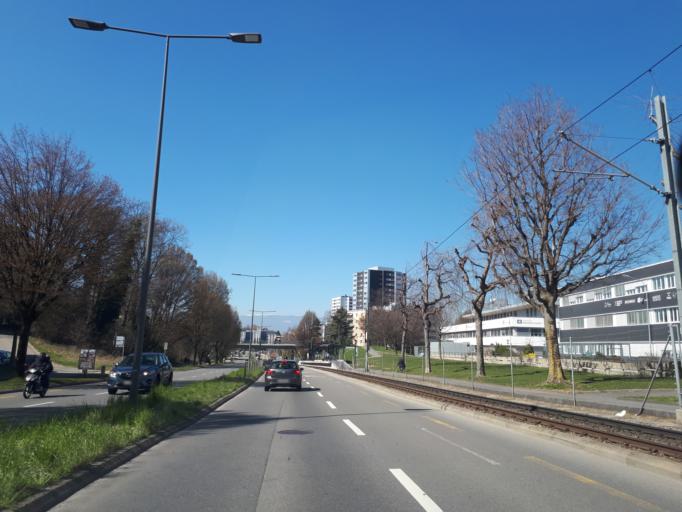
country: CH
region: Vaud
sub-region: Lausanne District
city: Blecherette
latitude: 46.5228
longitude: 6.6102
